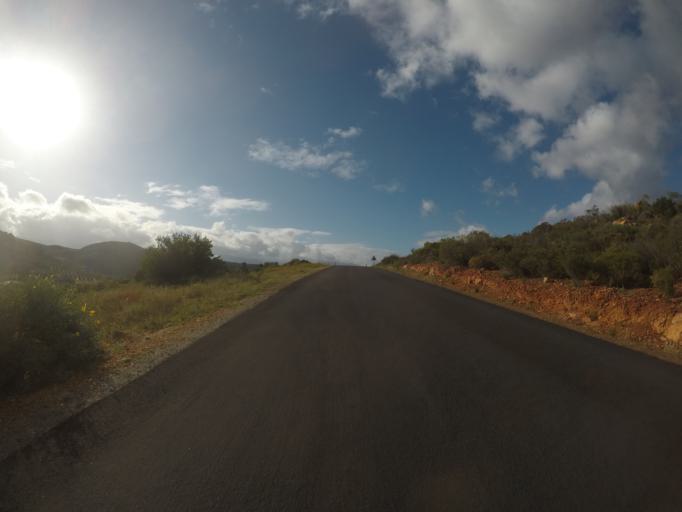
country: ZA
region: Western Cape
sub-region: West Coast District Municipality
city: Clanwilliam
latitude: -32.4216
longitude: 18.9325
